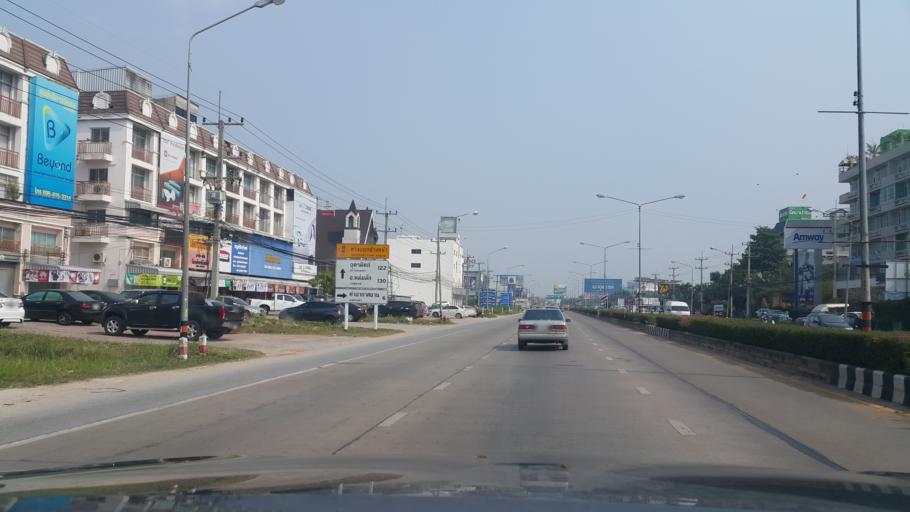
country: TH
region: Phitsanulok
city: Phitsanulok
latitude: 16.8196
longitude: 100.2823
